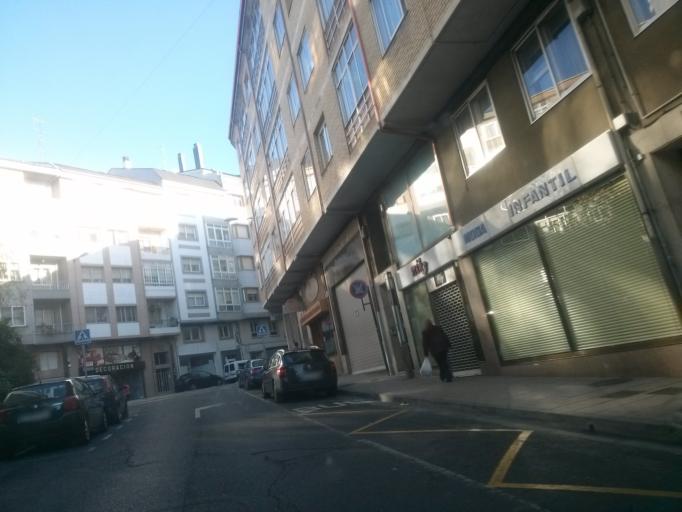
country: ES
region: Galicia
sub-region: Provincia de Lugo
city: Lugo
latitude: 43.0132
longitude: -7.5632
